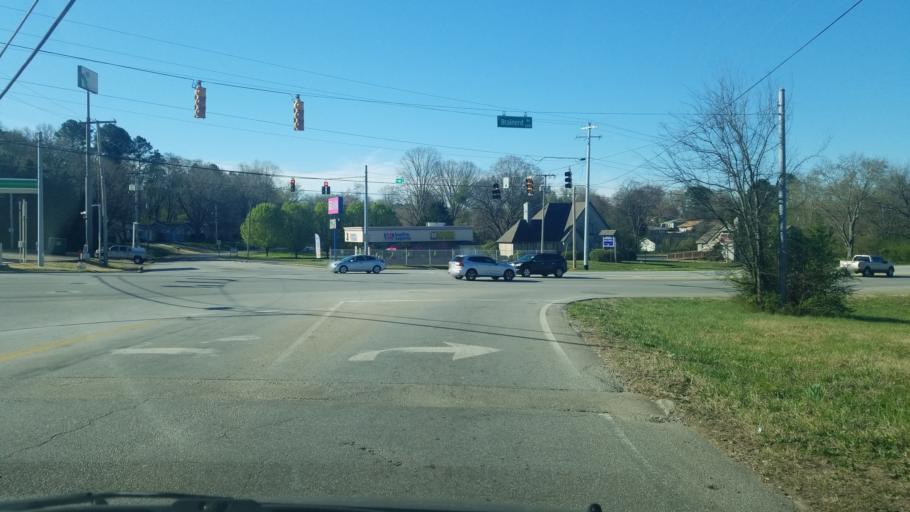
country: US
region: Tennessee
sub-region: Hamilton County
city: East Brainerd
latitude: 35.0183
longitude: -85.1738
